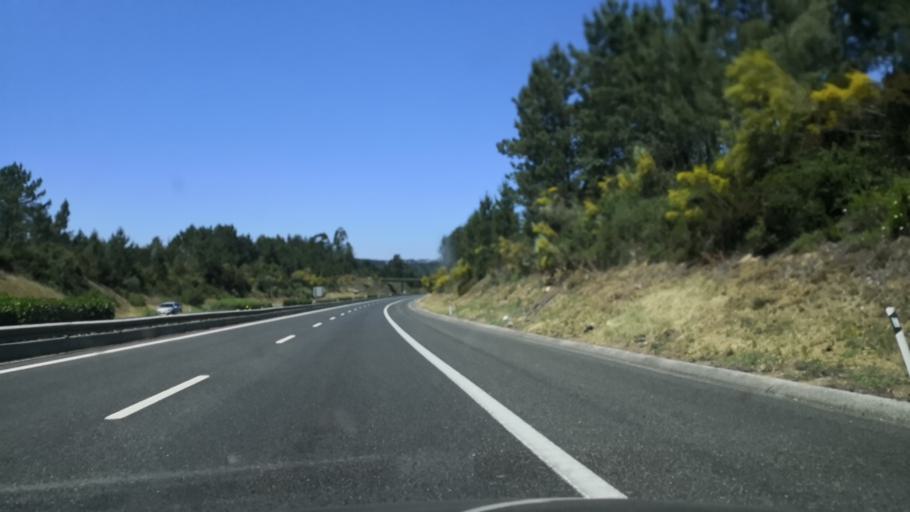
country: PT
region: Leiria
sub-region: Leiria
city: Santa Catarina da Serra
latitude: 39.7035
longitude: -8.7022
